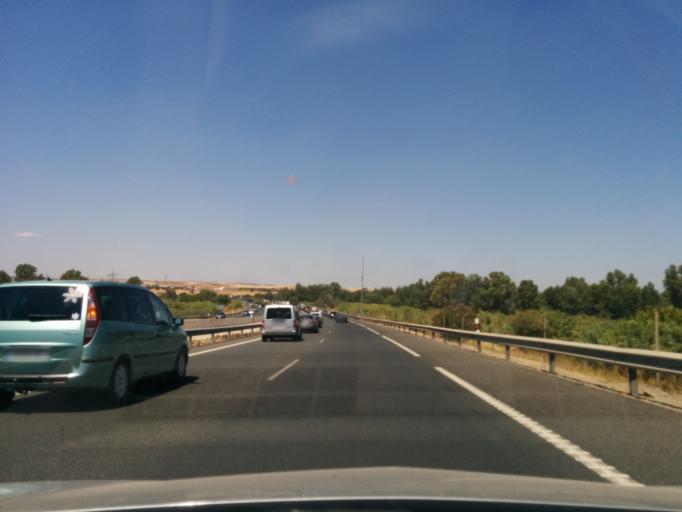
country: ES
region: Andalusia
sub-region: Provincia de Sevilla
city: Sanlucar la Mayor
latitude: 37.3707
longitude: -6.2223
